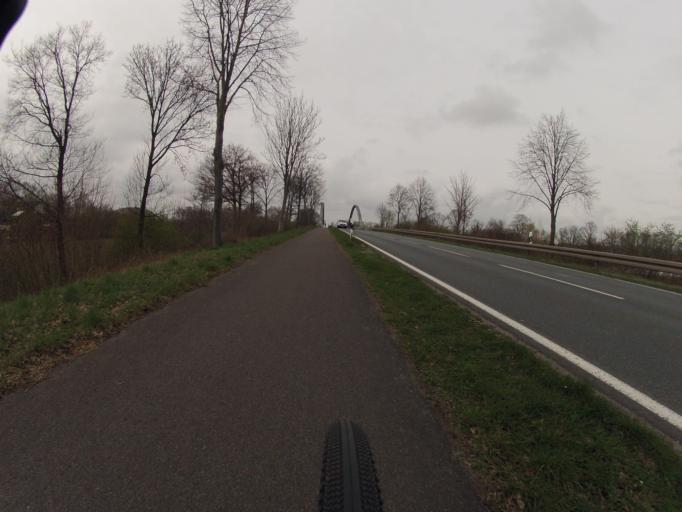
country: DE
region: North Rhine-Westphalia
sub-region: Regierungsbezirk Munster
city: Recke
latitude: 52.3555
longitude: 7.7237
